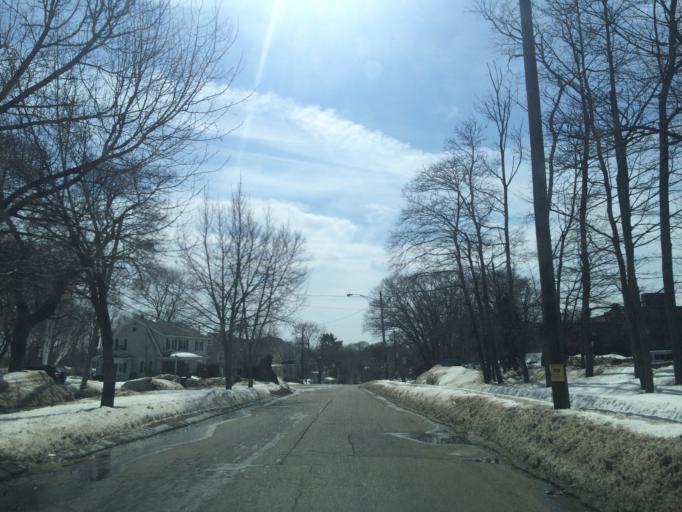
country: US
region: Massachusetts
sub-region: Middlesex County
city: Medford
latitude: 42.4272
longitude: -71.1104
